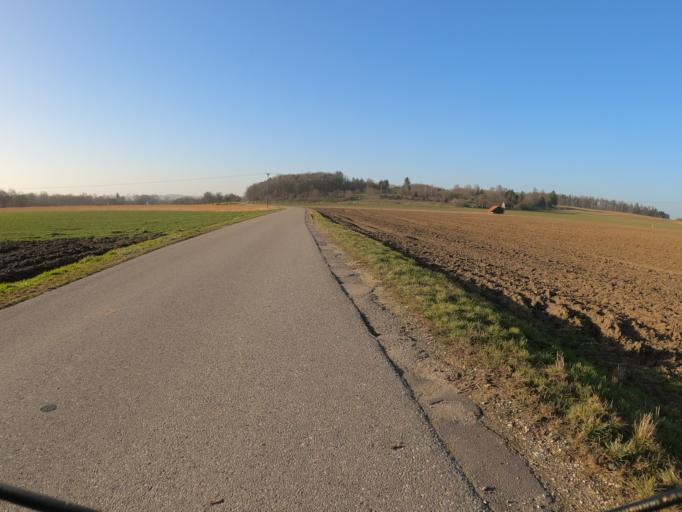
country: DE
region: Bavaria
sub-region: Swabia
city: Holzheim
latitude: 48.4028
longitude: 10.1032
